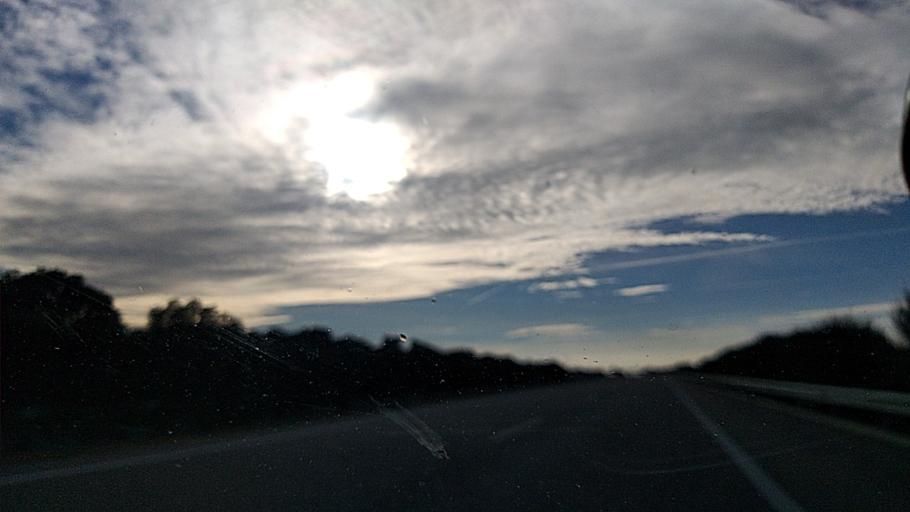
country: ES
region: Castille and Leon
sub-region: Provincia de Salamanca
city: Espeja
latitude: 40.5900
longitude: -6.7241
